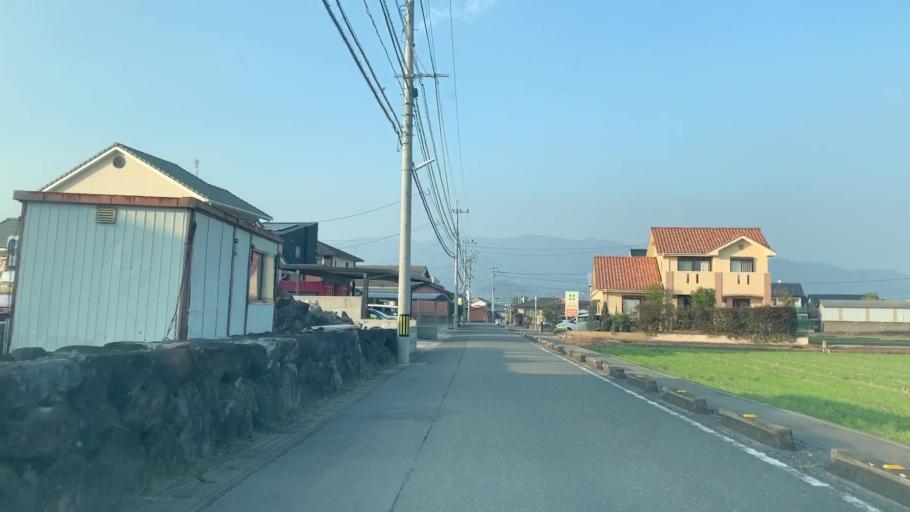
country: JP
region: Saga Prefecture
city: Saga-shi
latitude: 33.2758
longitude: 130.2271
